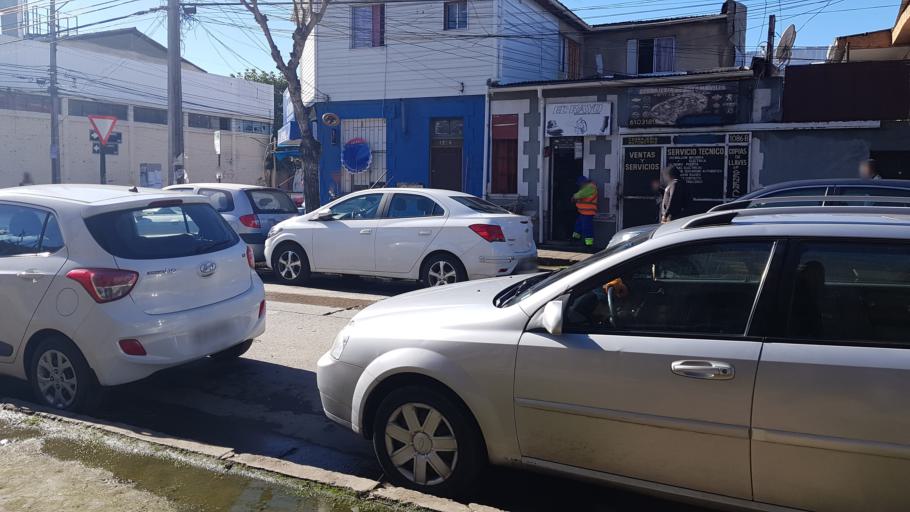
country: CL
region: Valparaiso
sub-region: Provincia de Valparaiso
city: Vina del Mar
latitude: -33.0123
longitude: -71.5443
